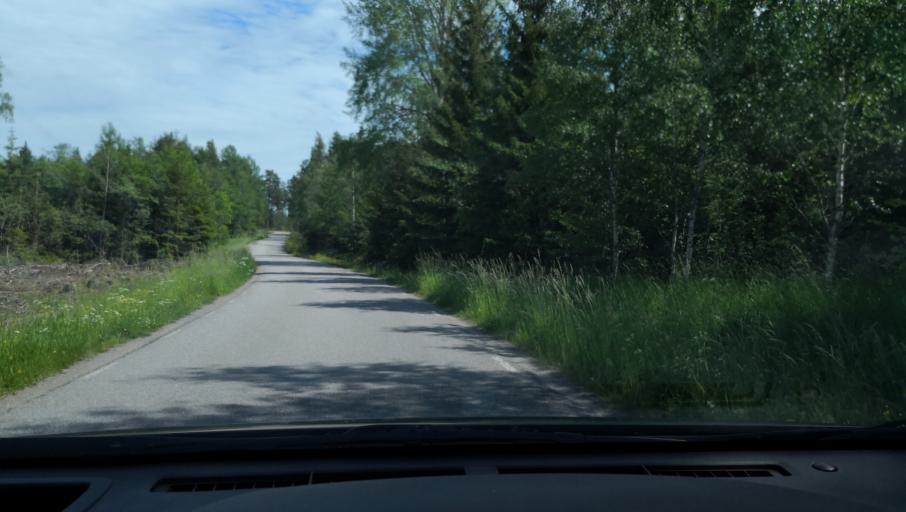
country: SE
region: Uppsala
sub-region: Uppsala Kommun
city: Alsike
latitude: 59.7062
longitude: 17.6719
